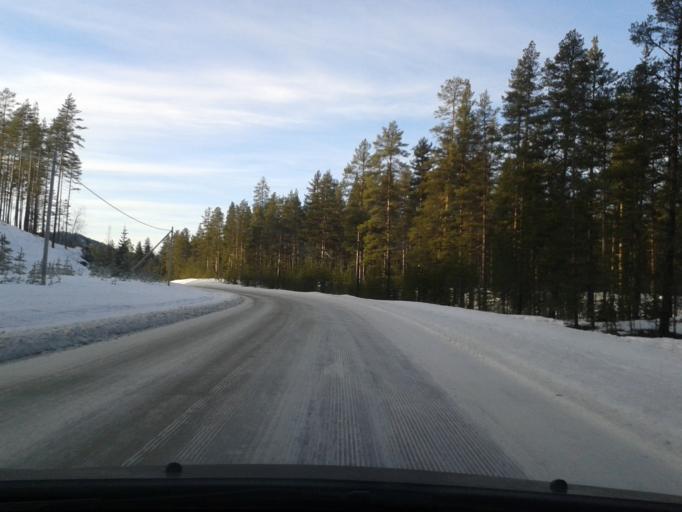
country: SE
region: Vaesternorrland
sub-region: OErnskoeldsviks Kommun
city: Bredbyn
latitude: 63.6747
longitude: 17.8159
